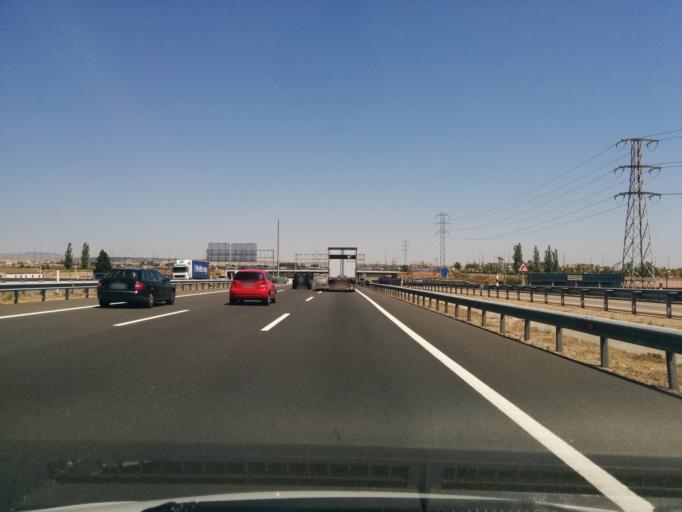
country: ES
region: Aragon
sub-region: Provincia de Zaragoza
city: Zaragoza
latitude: 41.6789
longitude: -0.8554
